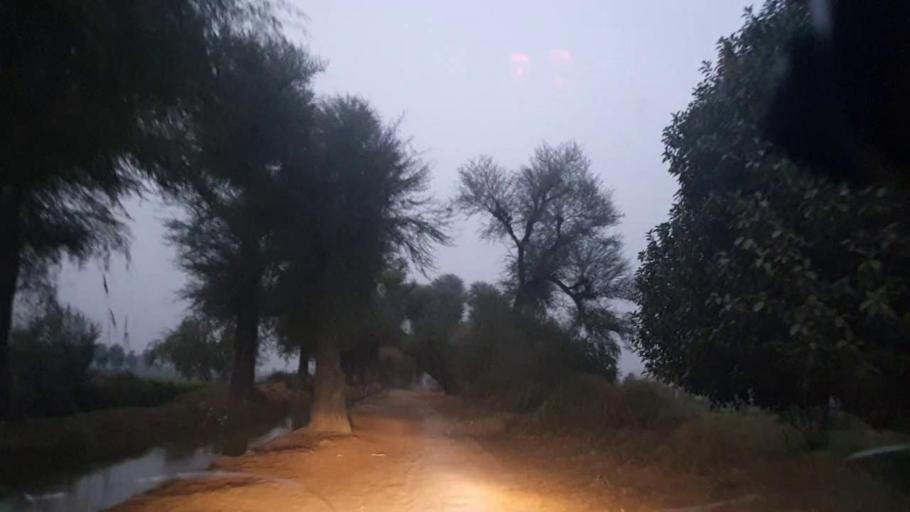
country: PK
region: Sindh
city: Hingorja
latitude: 27.2005
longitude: 68.3716
